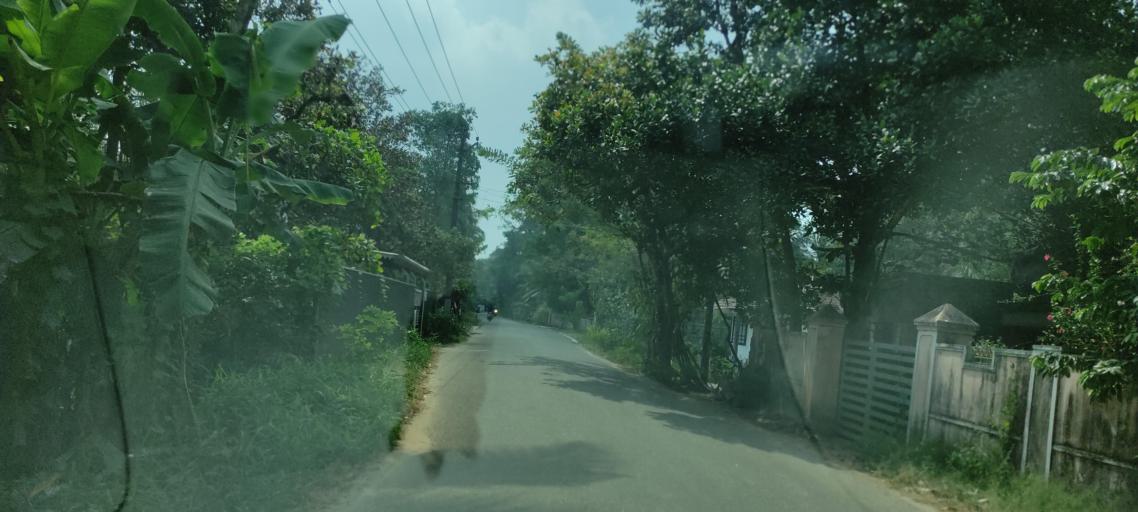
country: IN
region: Kerala
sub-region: Alappuzha
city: Shertallai
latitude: 9.6067
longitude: 76.3444
